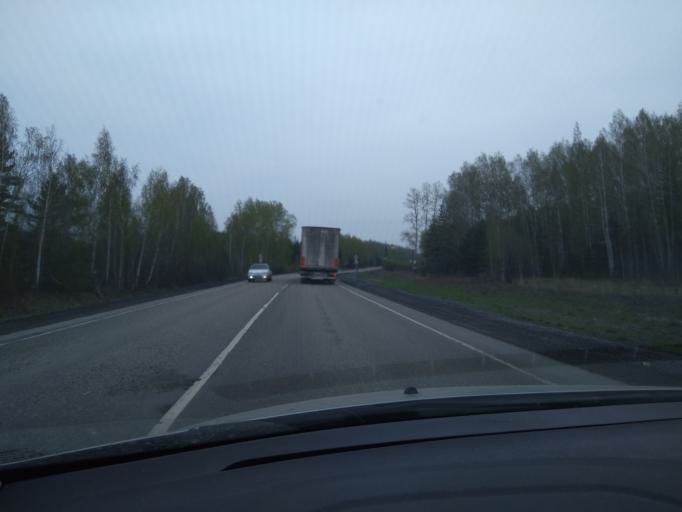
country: RU
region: Sverdlovsk
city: Zarechnyy
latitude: 56.7454
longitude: 61.2878
